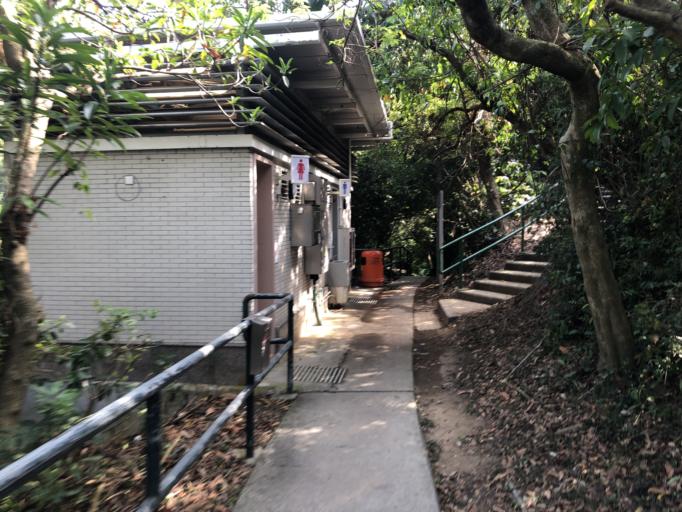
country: HK
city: Sok Kwu Wan
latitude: 22.2045
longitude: 114.1248
